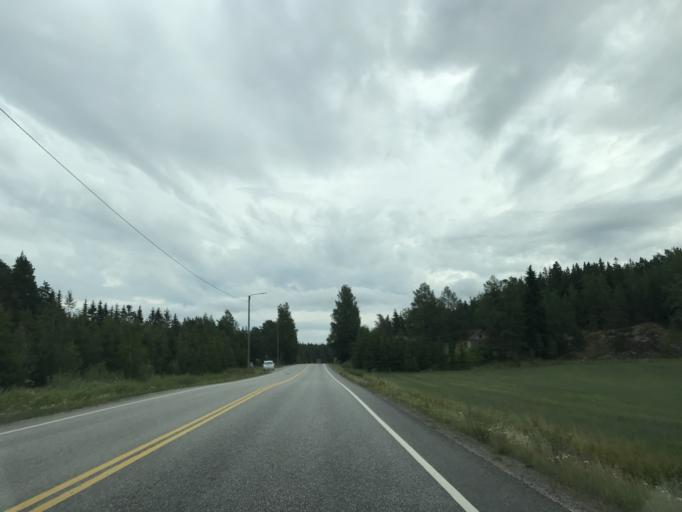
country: FI
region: Varsinais-Suomi
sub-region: Turku
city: Piikkioe
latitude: 60.4323
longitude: 22.6024
